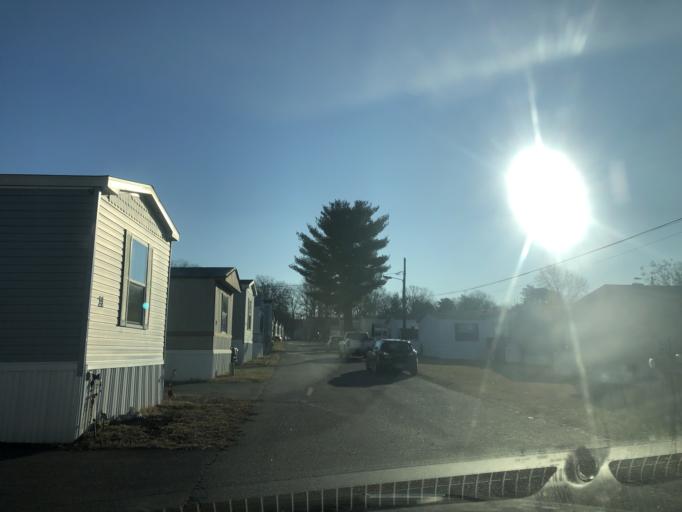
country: US
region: Maryland
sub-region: Anne Arundel County
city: Odenton
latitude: 39.0805
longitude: -76.7097
